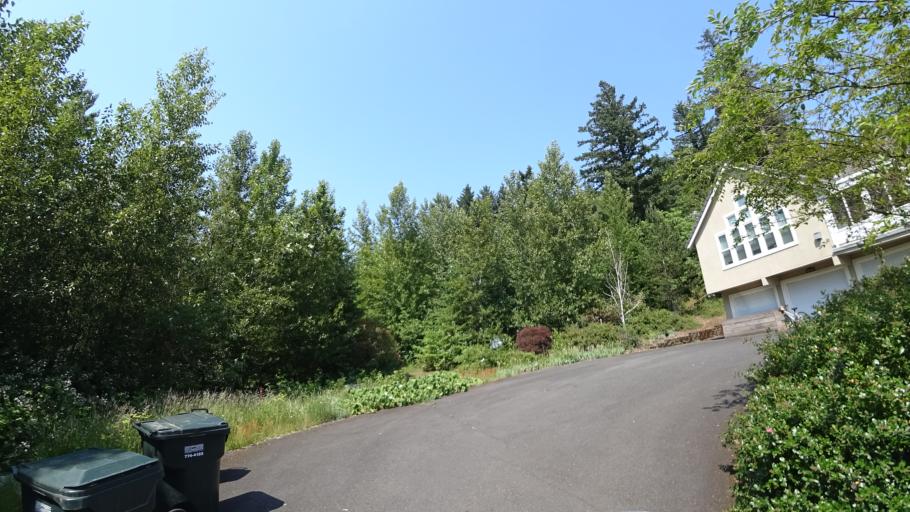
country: US
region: Oregon
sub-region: Clackamas County
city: Happy Valley
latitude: 45.4446
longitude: -122.5566
